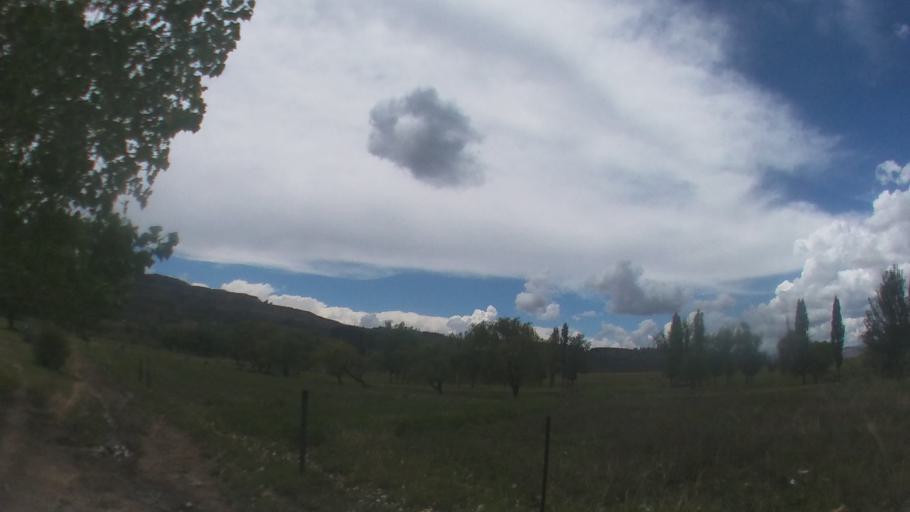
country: LS
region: Maseru
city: Nako
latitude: -29.6181
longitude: 27.5067
